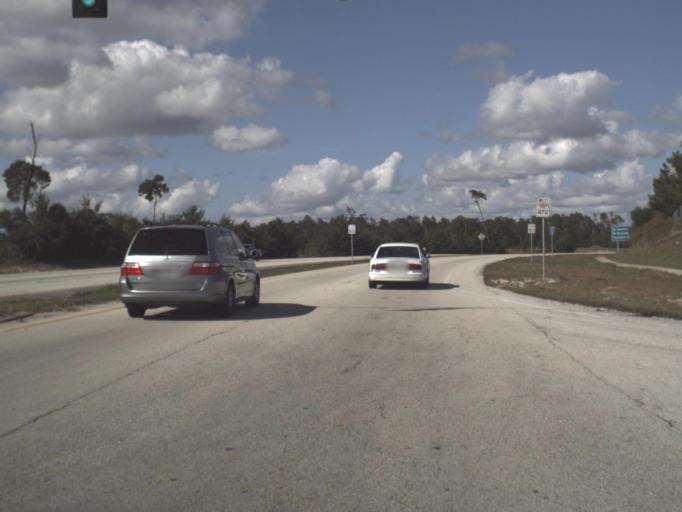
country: US
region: Florida
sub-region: Volusia County
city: Lake Helen
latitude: 28.9494
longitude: -81.2519
